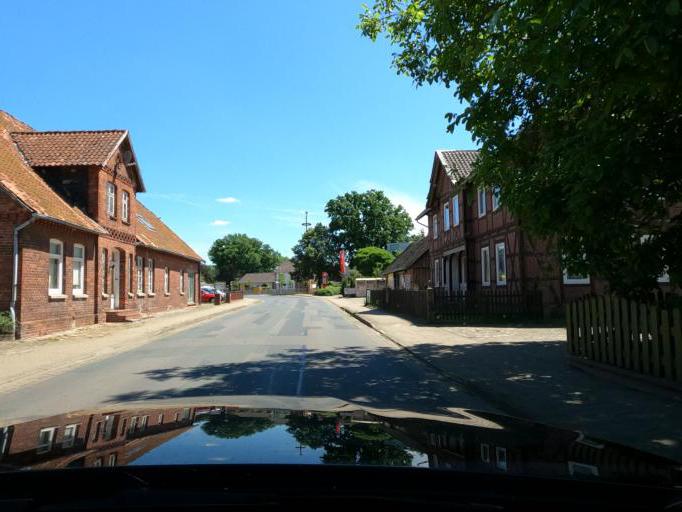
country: DE
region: Lower Saxony
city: Muden
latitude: 52.5260
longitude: 10.3615
